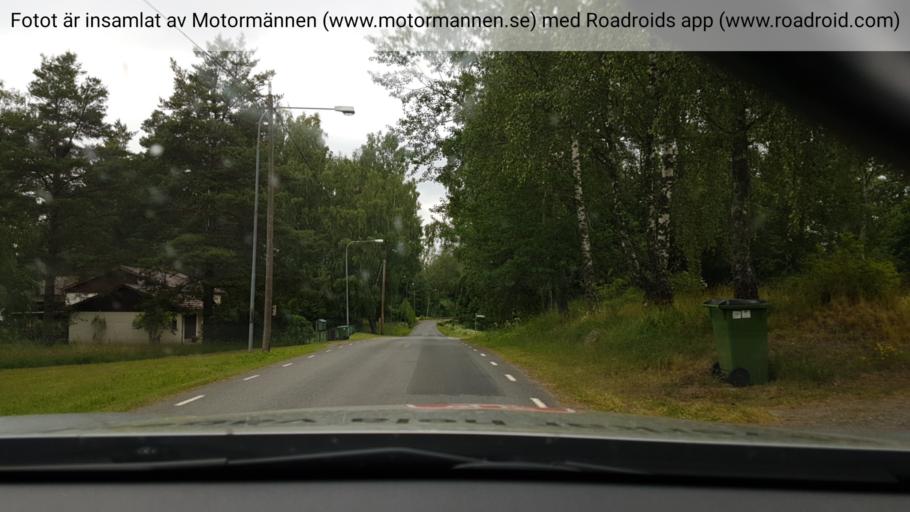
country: SE
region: Joenkoeping
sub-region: Mullsjo Kommun
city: Mullsjoe
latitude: 57.9880
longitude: 13.7830
